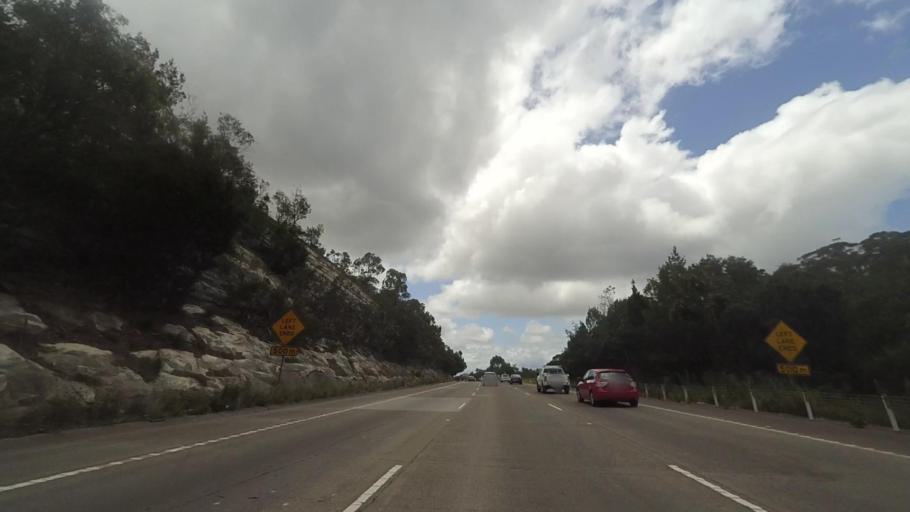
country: AU
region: New South Wales
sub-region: Gosford Shire
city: Point Clare
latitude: -33.4097
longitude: 151.2987
